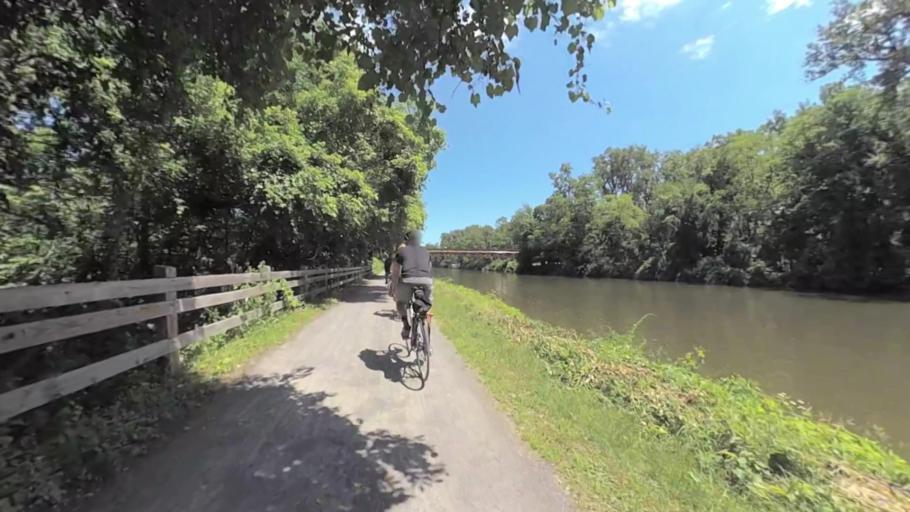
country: US
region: New York
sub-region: Monroe County
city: Fairport
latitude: 43.0758
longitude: -77.4635
